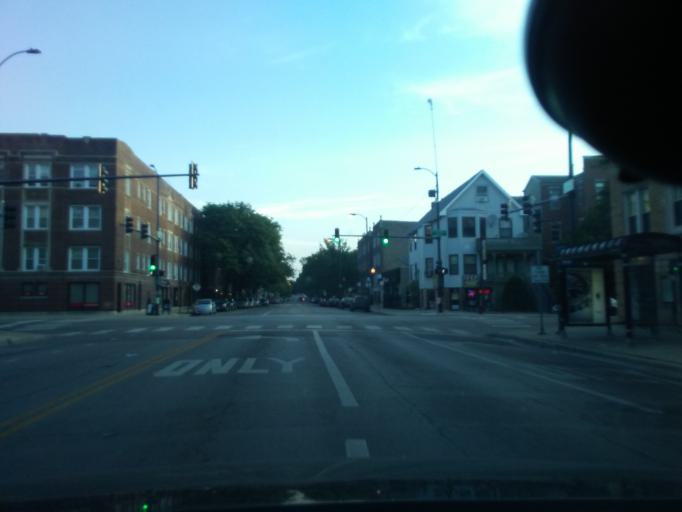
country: US
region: Illinois
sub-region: Cook County
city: Lincolnwood
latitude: 41.9757
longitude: -87.6794
